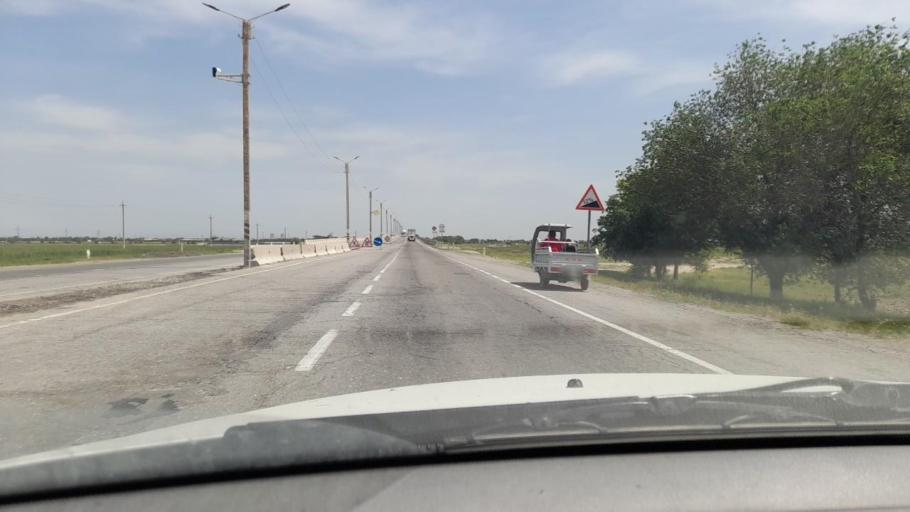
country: UZ
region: Navoiy
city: Beshrabot
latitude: 40.1316
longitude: 65.2154
